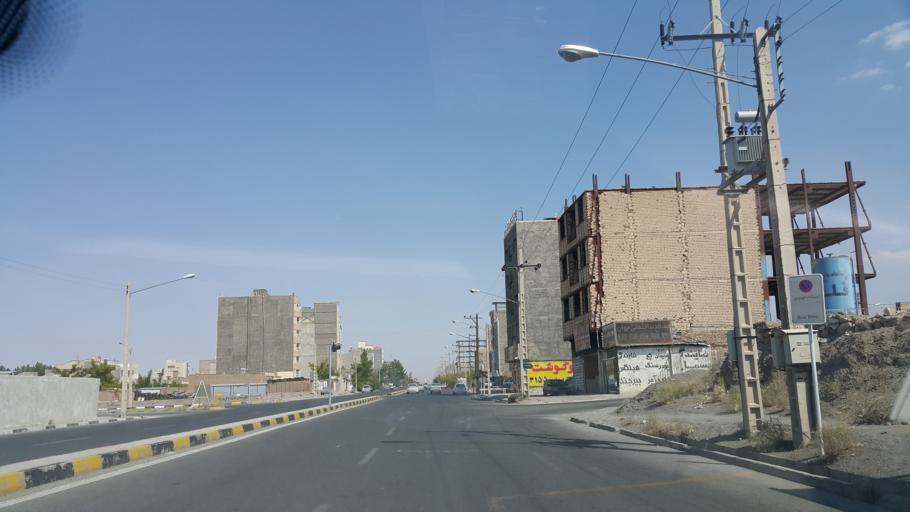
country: IR
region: Khorasan-e Jonubi
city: Birjand
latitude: 32.8461
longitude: 59.2111
